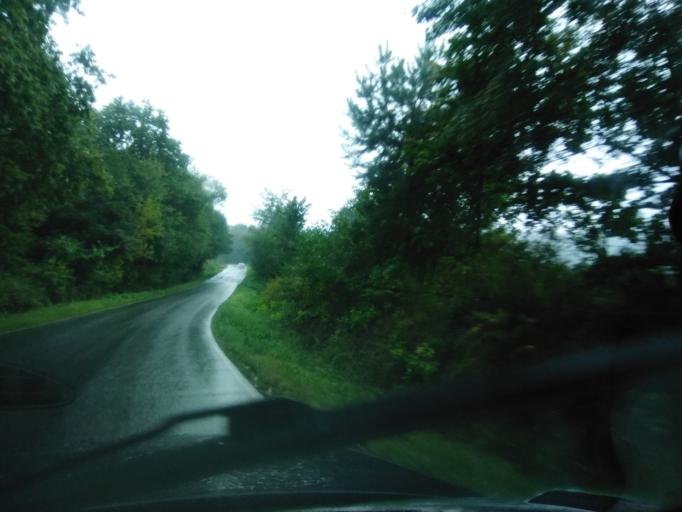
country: PL
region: Subcarpathian Voivodeship
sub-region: Powiat ropczycko-sedziszowski
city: Niedzwiada
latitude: 50.0417
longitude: 21.5441
